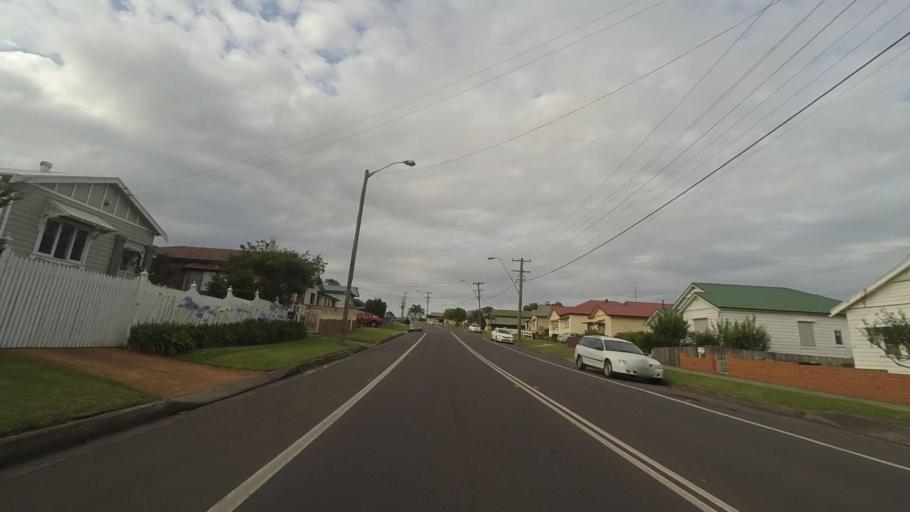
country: AU
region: New South Wales
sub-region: Wollongong
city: Wollongong
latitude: -34.4334
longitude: 150.8860
